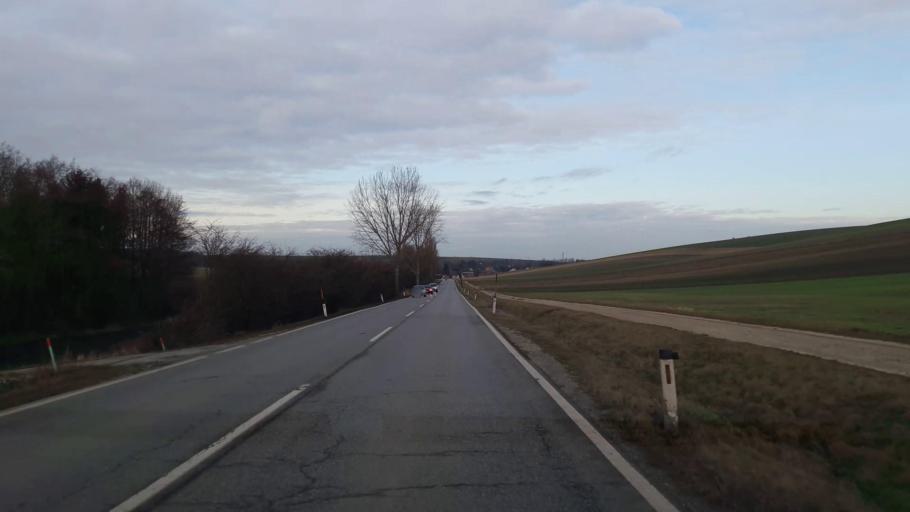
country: AT
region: Lower Austria
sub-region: Politischer Bezirk Mistelbach
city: Staatz
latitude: 48.6529
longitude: 16.5033
